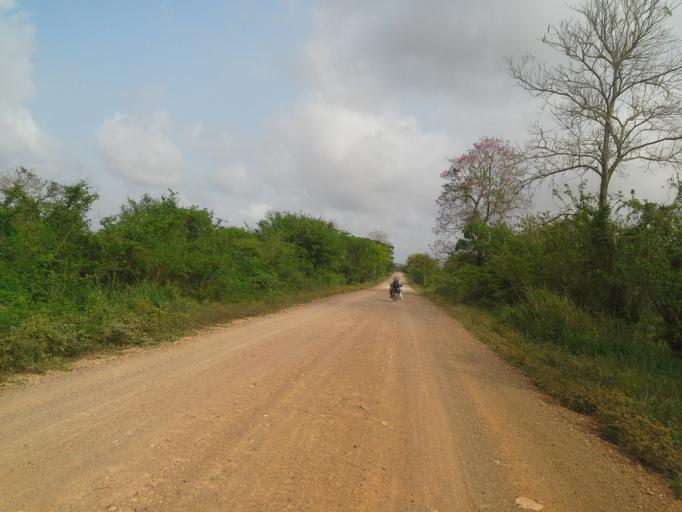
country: CO
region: Cordoba
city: Chima
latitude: 9.1381
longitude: -75.6121
